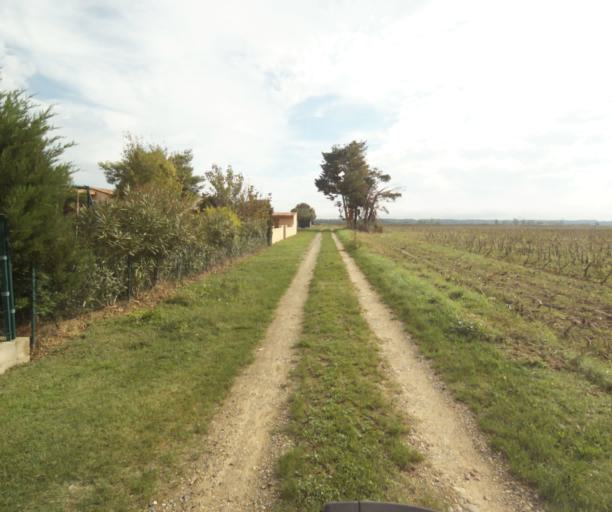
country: FR
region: Midi-Pyrenees
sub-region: Departement du Tarn-et-Garonne
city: Finhan
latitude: 43.9121
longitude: 1.2281
